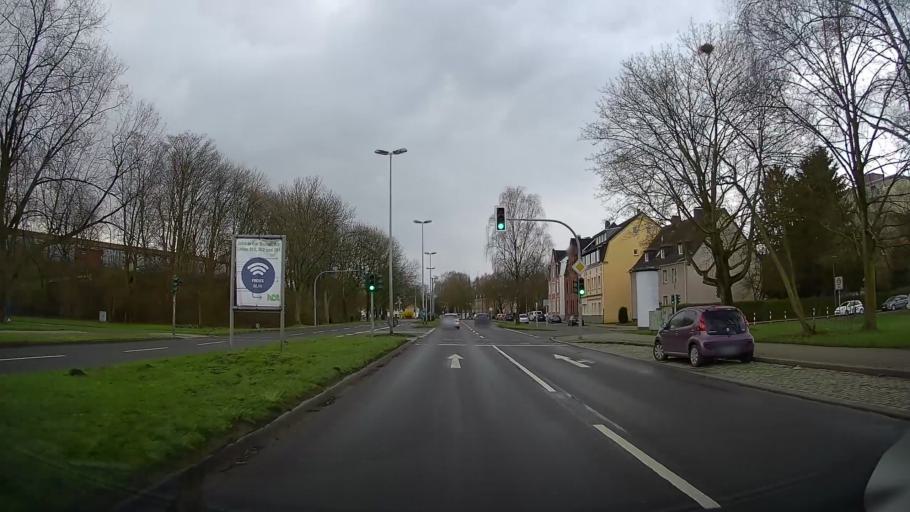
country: DE
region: North Rhine-Westphalia
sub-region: Regierungsbezirk Arnsberg
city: Herne
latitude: 51.5525
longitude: 7.2065
